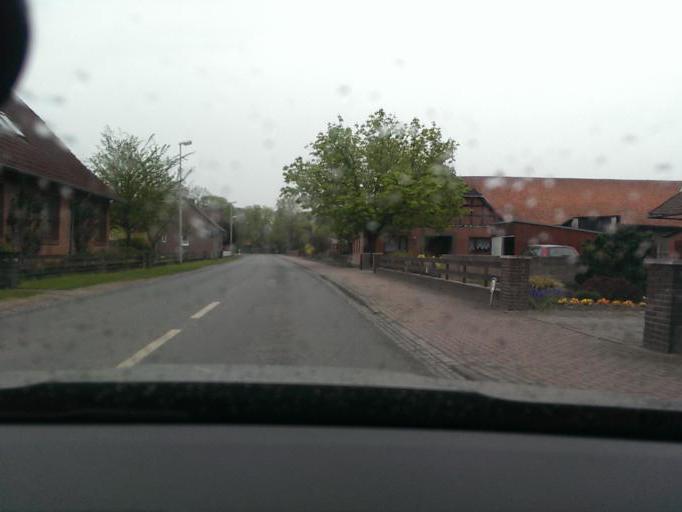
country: DE
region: Lower Saxony
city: Gilten
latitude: 52.6387
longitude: 9.5019
